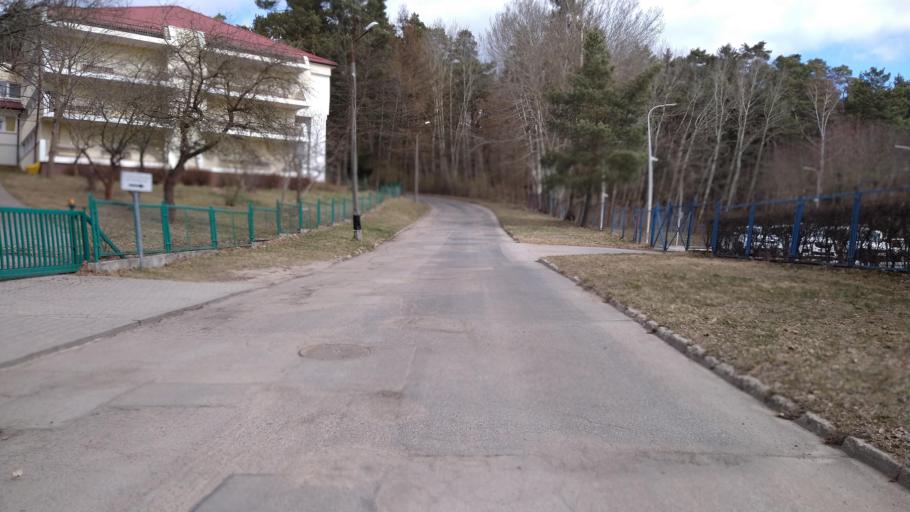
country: PL
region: Warmian-Masurian Voivodeship
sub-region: Powiat olsztynski
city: Olsztyn
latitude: 53.8016
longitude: 20.4911
